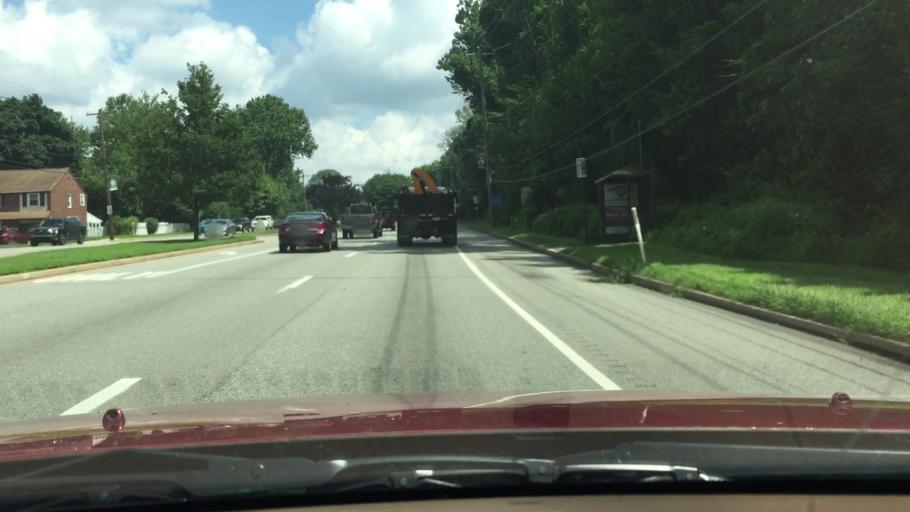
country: US
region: Pennsylvania
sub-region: Delaware County
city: Broomall
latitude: 39.9759
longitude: -75.3315
